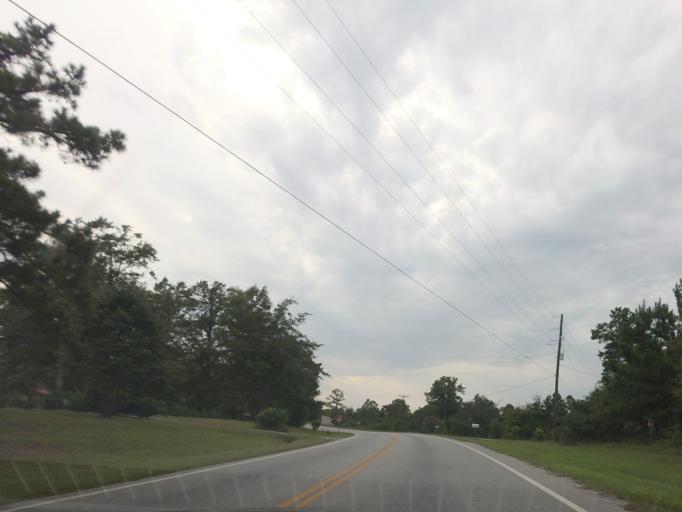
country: US
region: Georgia
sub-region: Twiggs County
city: Jeffersonville
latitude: 32.7607
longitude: -83.4456
